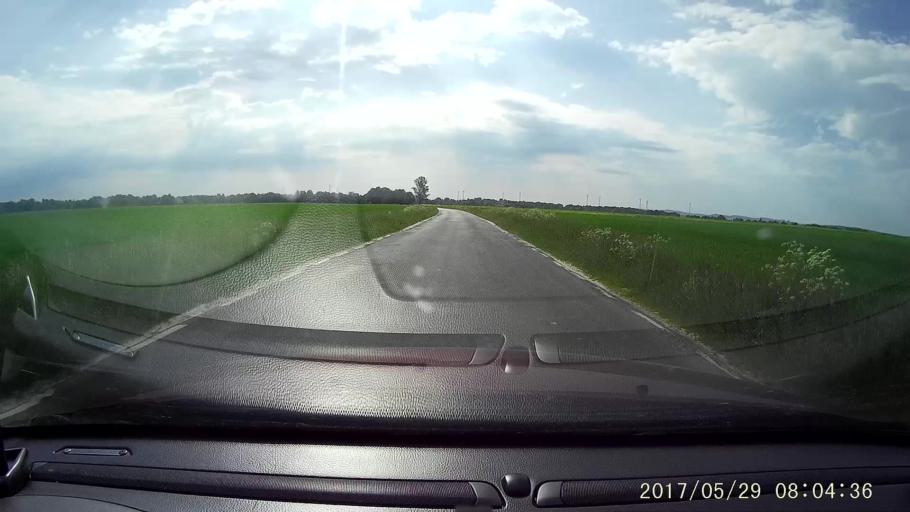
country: PL
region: Lower Silesian Voivodeship
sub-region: Powiat zlotoryjski
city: Zagrodno
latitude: 51.1966
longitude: 15.8493
